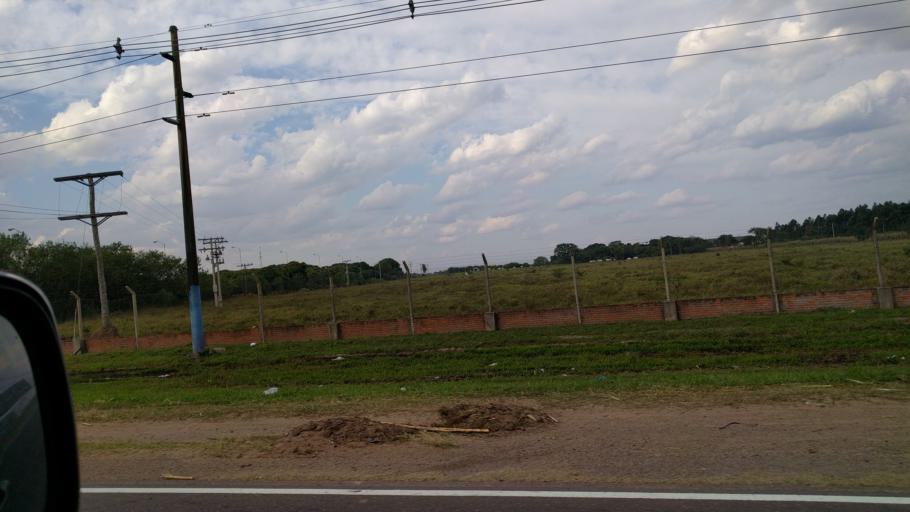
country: BO
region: Santa Cruz
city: La Belgica
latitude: -17.5575
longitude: -63.1595
